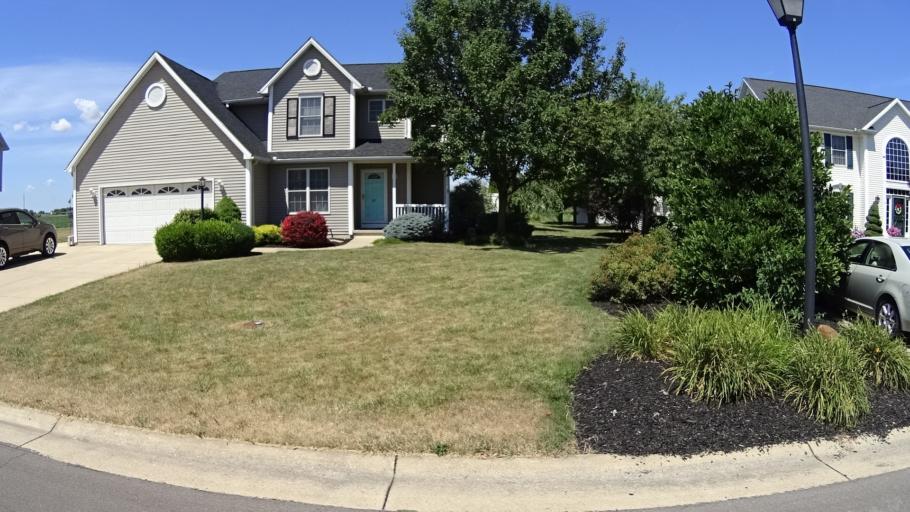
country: US
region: Ohio
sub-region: Erie County
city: Sandusky
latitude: 41.4039
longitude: -82.6958
